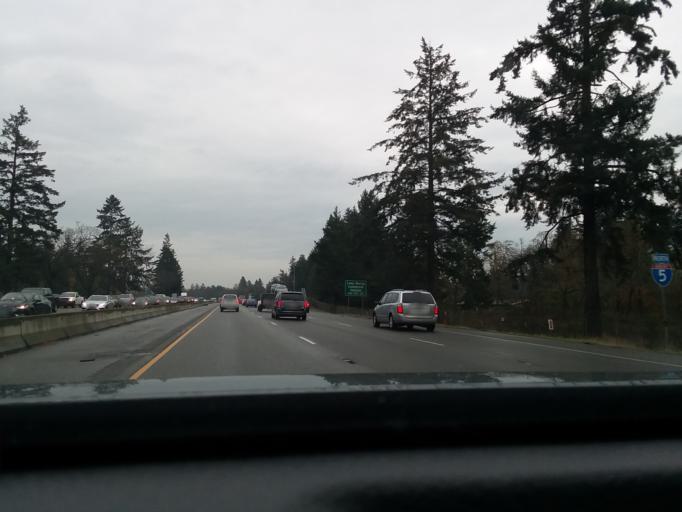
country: US
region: Washington
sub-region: Pierce County
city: Fort Lewis
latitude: 47.1086
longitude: -122.5771
